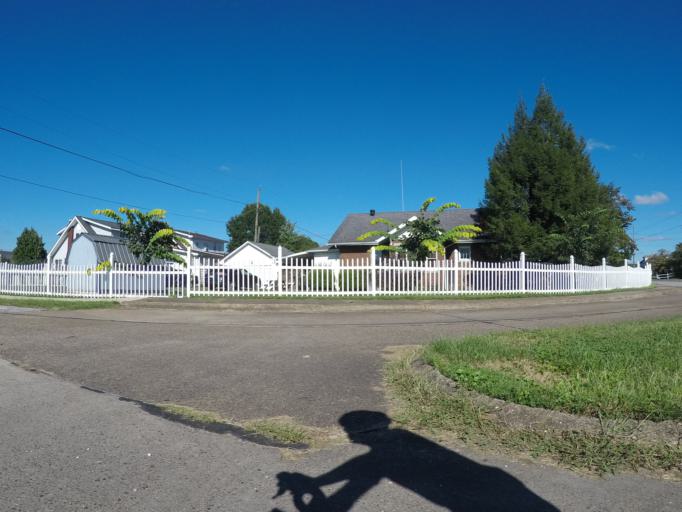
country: US
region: Ohio
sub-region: Lawrence County
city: Burlington
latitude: 38.4027
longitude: -82.5060
